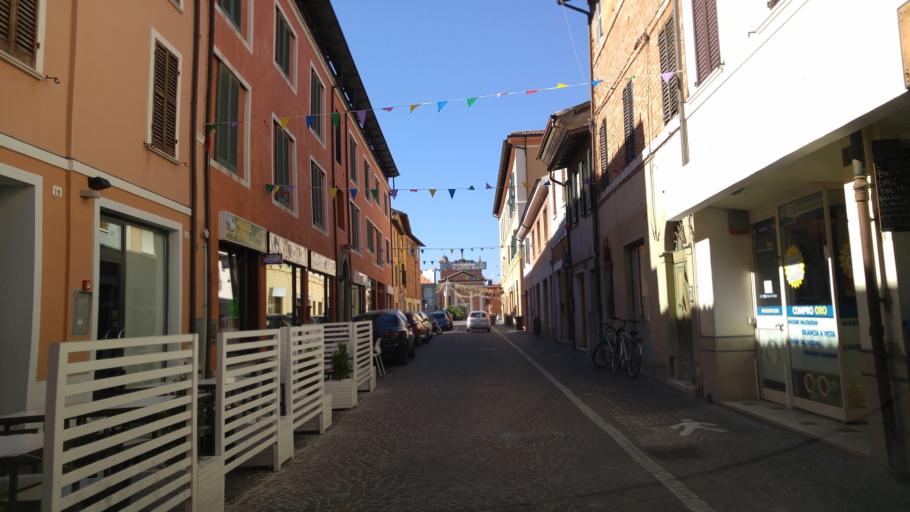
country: IT
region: The Marches
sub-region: Provincia di Pesaro e Urbino
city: Pesaro
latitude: 43.9127
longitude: 12.9082
